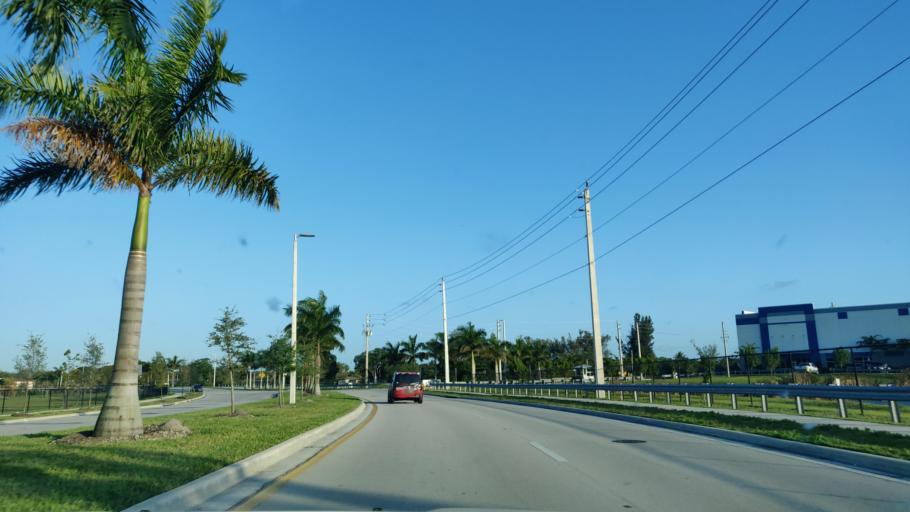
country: US
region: Florida
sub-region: Miami-Dade County
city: Westview
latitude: 25.8806
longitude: -80.2381
